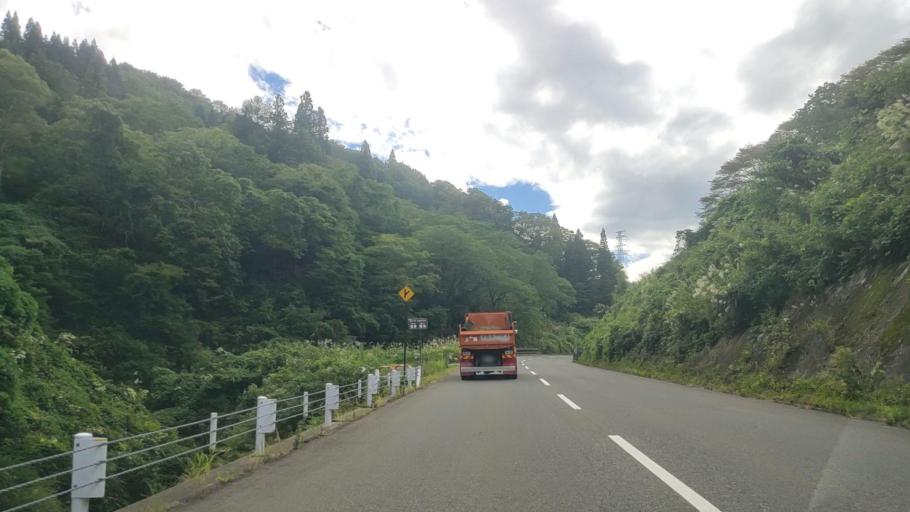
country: JP
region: Nagano
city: Iiyama
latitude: 36.8965
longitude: 138.3208
